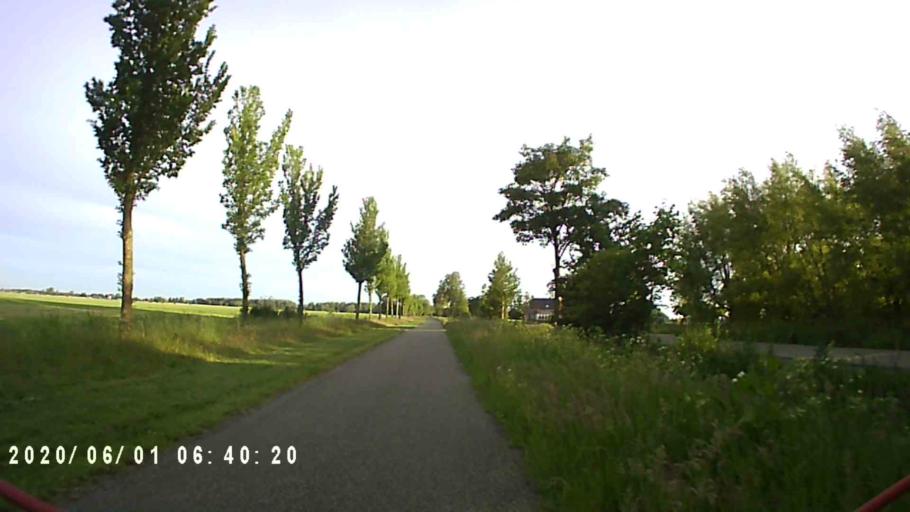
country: NL
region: Friesland
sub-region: Gemeente Kollumerland en Nieuwkruisland
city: Kollum
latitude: 53.2924
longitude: 6.1575
